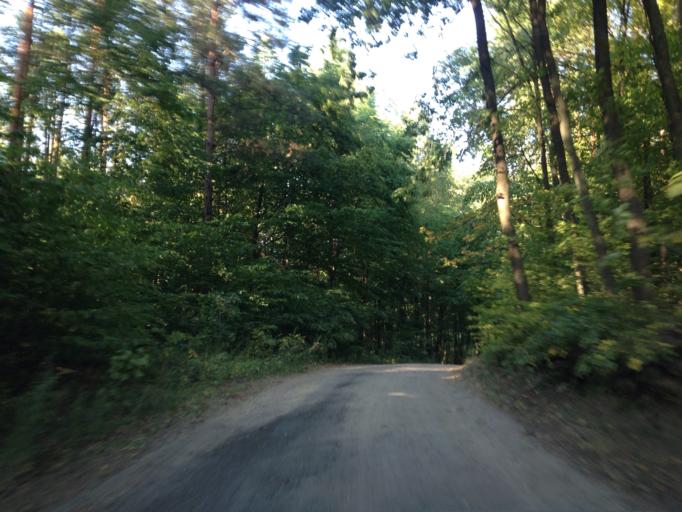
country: PL
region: Warmian-Masurian Voivodeship
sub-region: Powiat dzialdowski
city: Lidzbark
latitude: 53.2323
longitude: 19.7455
